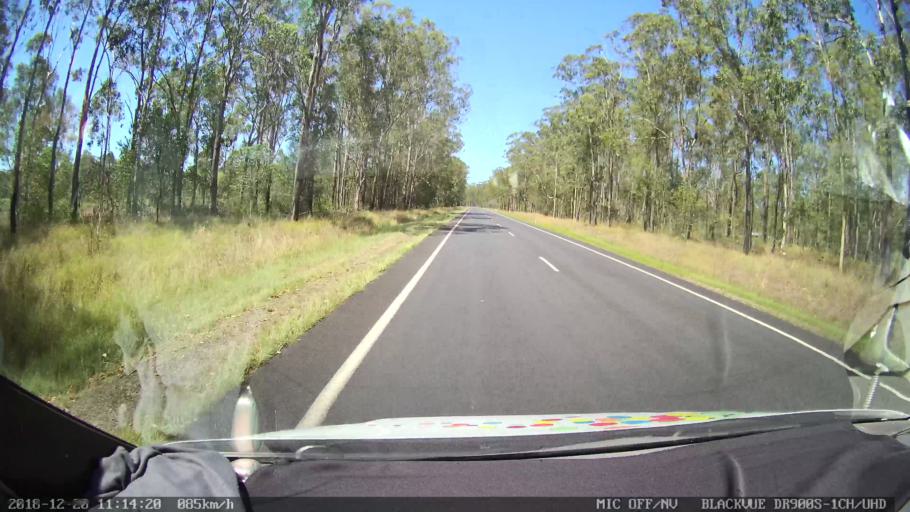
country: AU
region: New South Wales
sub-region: Richmond Valley
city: Casino
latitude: -28.9993
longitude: 153.0093
